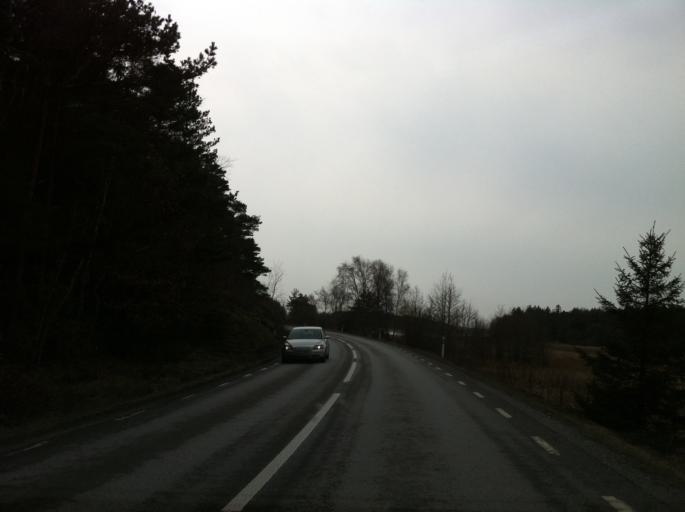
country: SE
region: Vaestra Goetaland
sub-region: Orust
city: Henan
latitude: 58.3087
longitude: 11.6983
